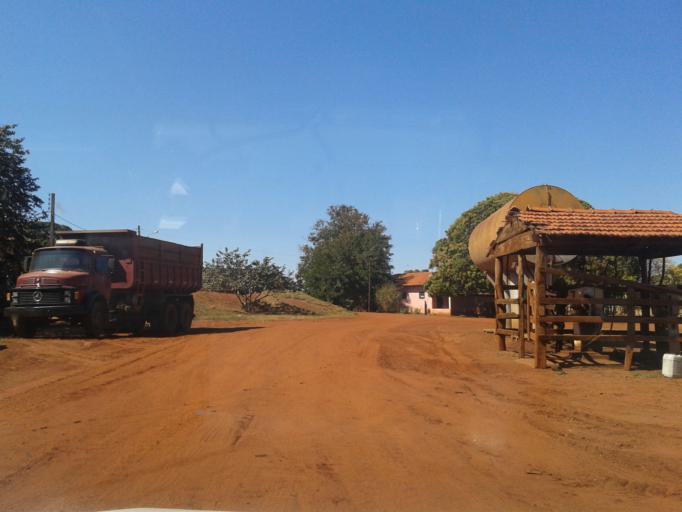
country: BR
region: Minas Gerais
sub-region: Santa Vitoria
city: Santa Vitoria
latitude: -19.2398
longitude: -50.2060
